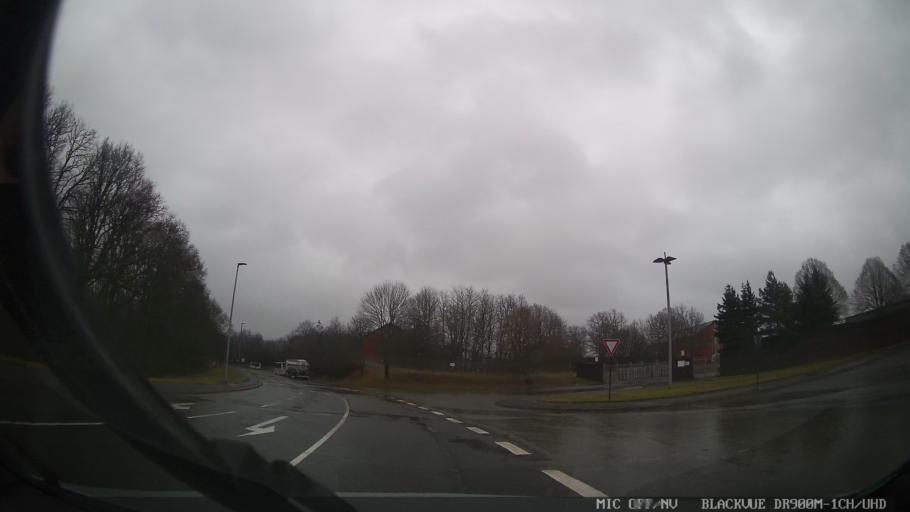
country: DE
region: Rheinland-Pfalz
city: Idar-Oberstein
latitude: 49.7107
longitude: 7.2983
